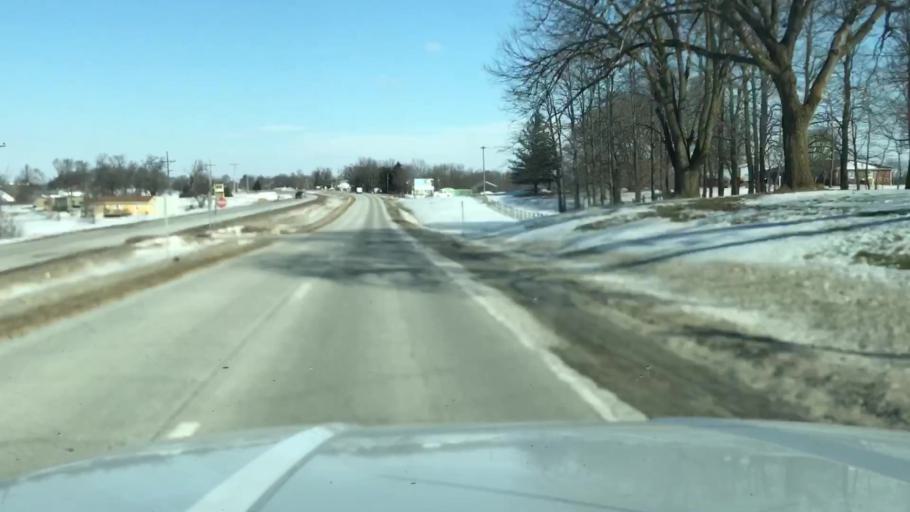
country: US
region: Missouri
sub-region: Andrew County
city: Savannah
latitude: 39.9048
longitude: -94.8097
